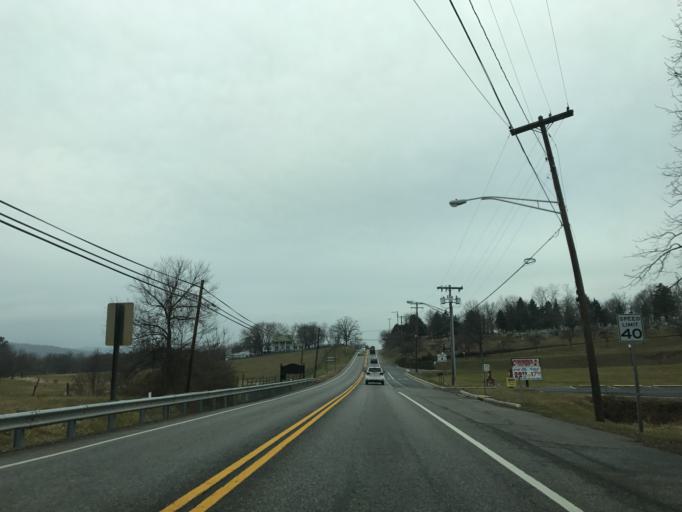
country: US
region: Maryland
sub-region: Frederick County
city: Emmitsburg
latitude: 39.7077
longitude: -77.3347
